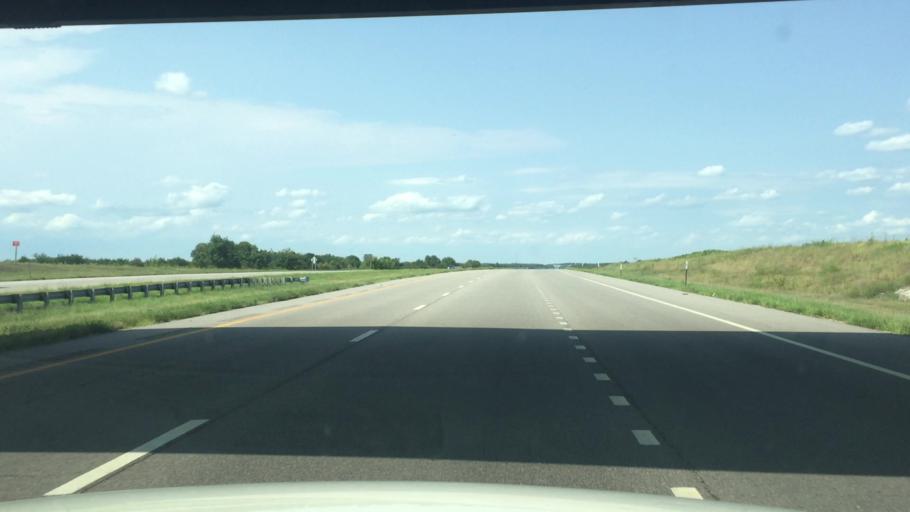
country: US
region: Kansas
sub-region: Linn County
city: La Cygne
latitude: 38.4033
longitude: -94.6877
